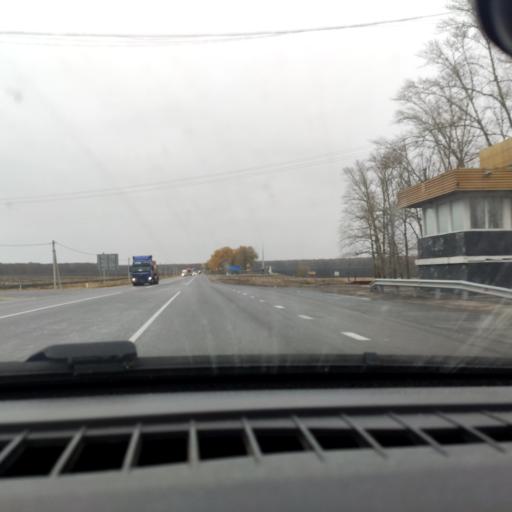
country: RU
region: Voronezj
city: Ostrogozhsk
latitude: 50.9026
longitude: 39.0670
